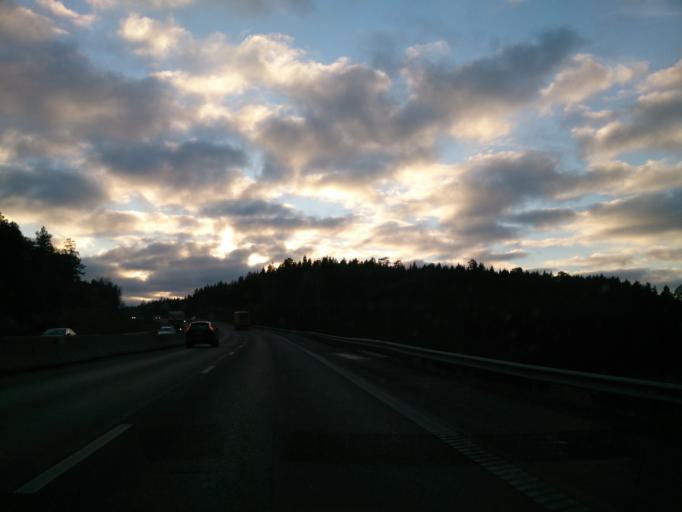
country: SE
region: OEstergoetland
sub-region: Norrkopings Kommun
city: Kimstad
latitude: 58.5472
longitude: 16.0473
